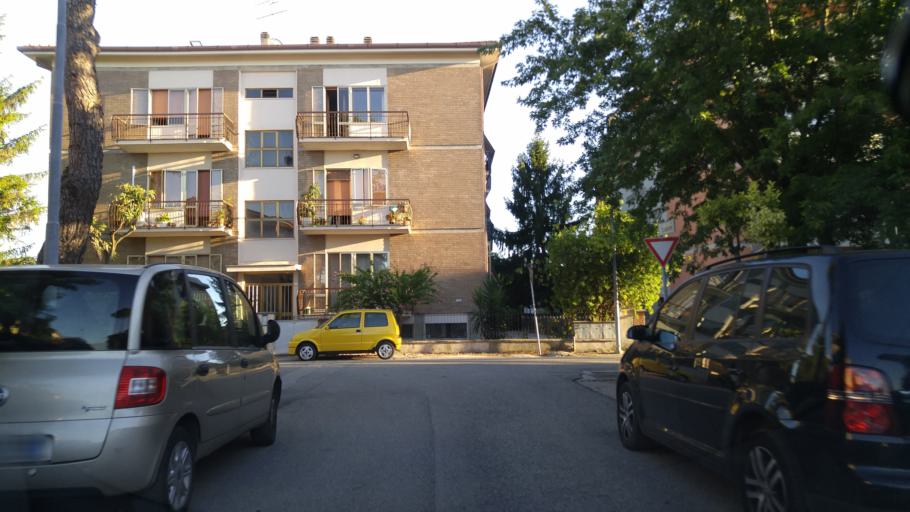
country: IT
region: The Marches
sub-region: Provincia di Pesaro e Urbino
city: Fano
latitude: 43.8339
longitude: 13.0230
